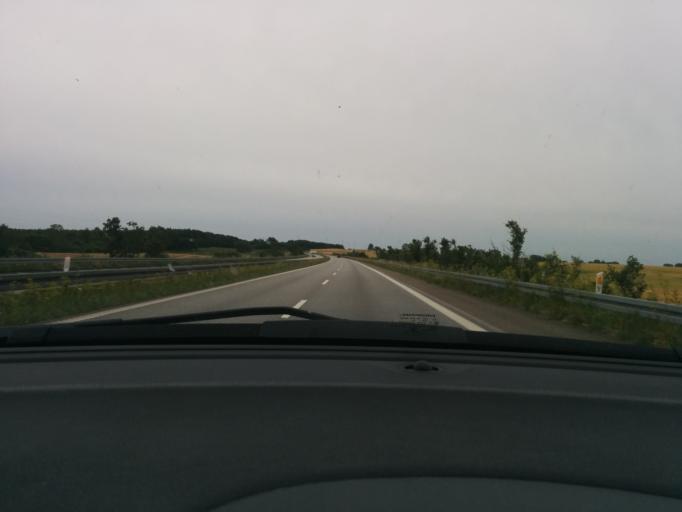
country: DK
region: Zealand
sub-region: Vordingborg Kommune
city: Orslev
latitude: 55.1017
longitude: 11.9366
